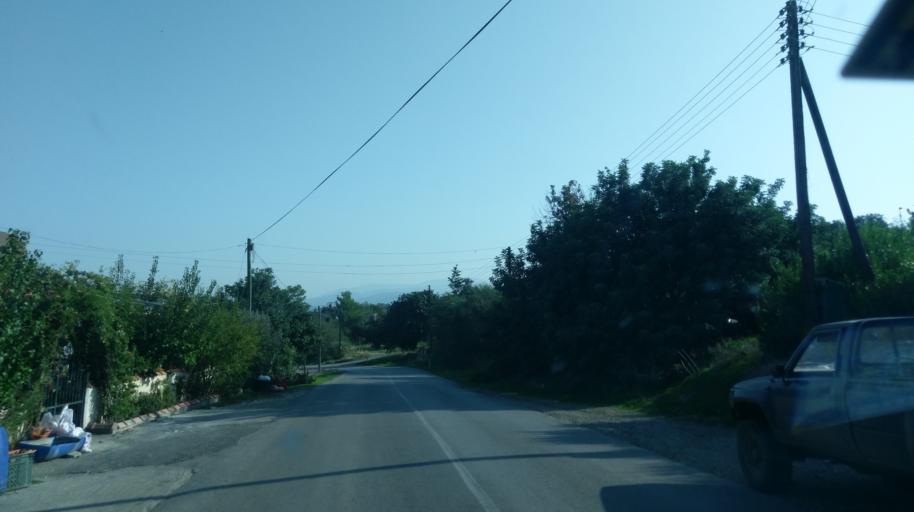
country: CY
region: Lefkosia
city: Kato Pyrgos
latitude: 35.1593
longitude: 32.7633
